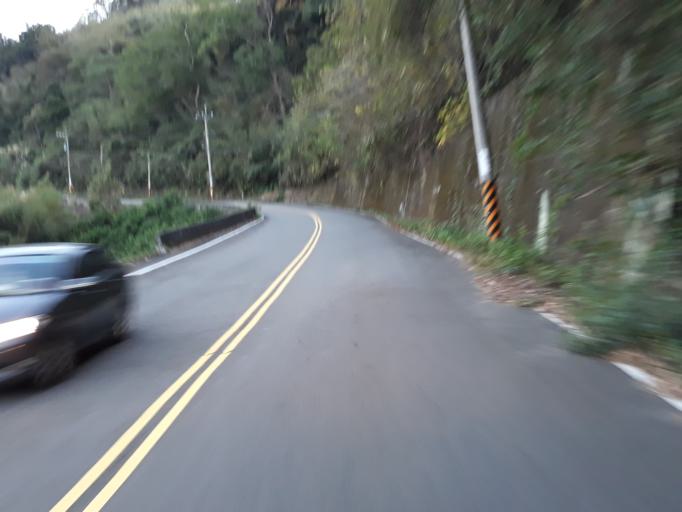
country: TW
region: Taiwan
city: Fengyuan
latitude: 24.3623
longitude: 120.8679
